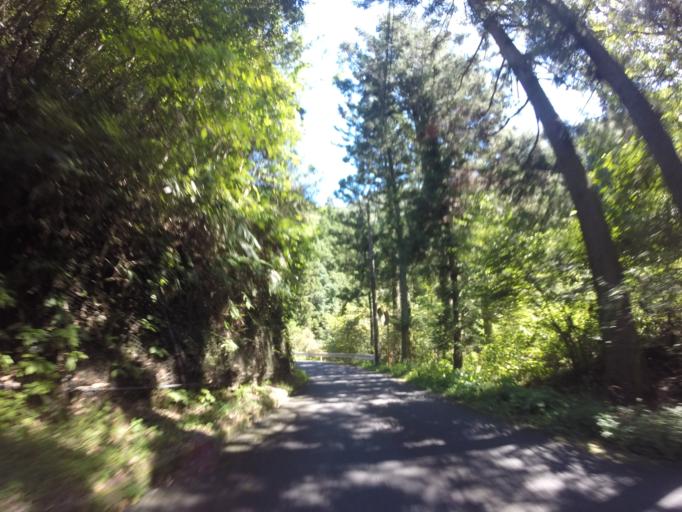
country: JP
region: Shizuoka
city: Fujieda
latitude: 34.9667
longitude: 138.1924
